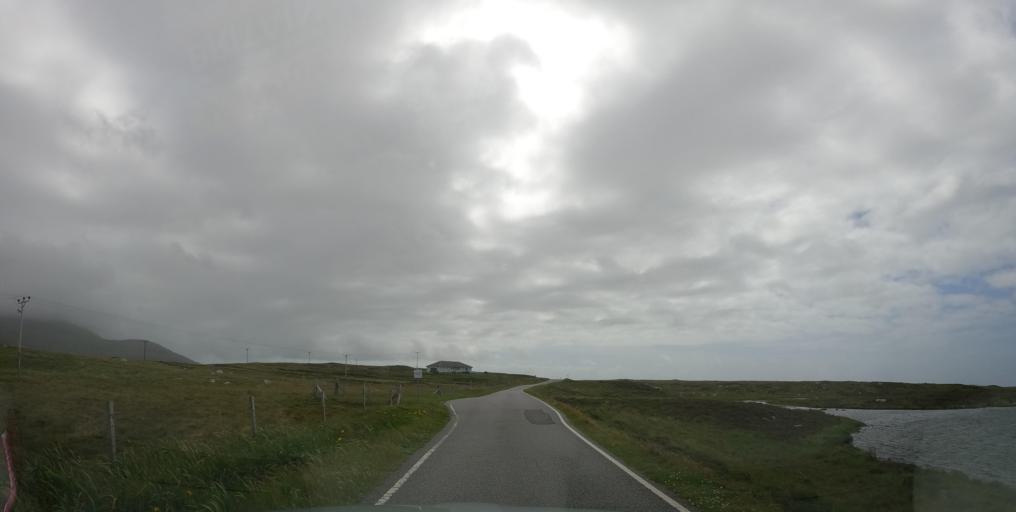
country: GB
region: Scotland
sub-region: Eilean Siar
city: Isle of South Uist
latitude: 57.2845
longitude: -7.3663
